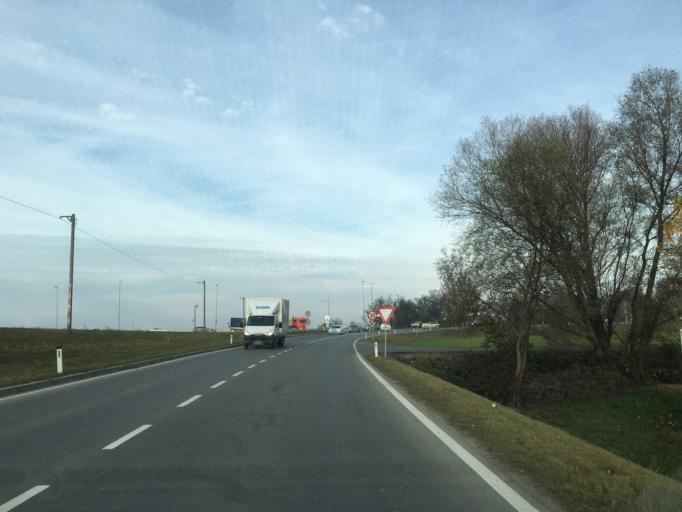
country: AT
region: Vorarlberg
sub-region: Politischer Bezirk Bregenz
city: Fussach
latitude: 47.4766
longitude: 9.6713
